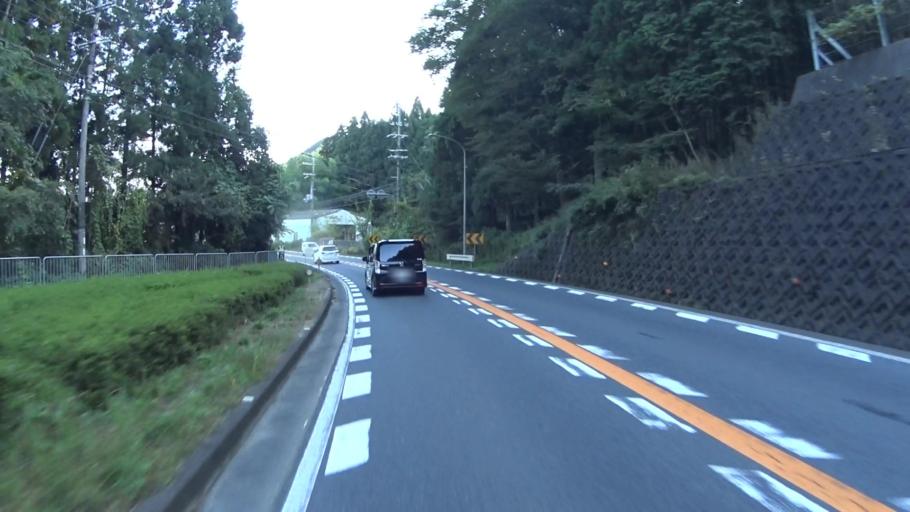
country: JP
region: Kyoto
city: Ayabe
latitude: 35.2332
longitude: 135.2183
